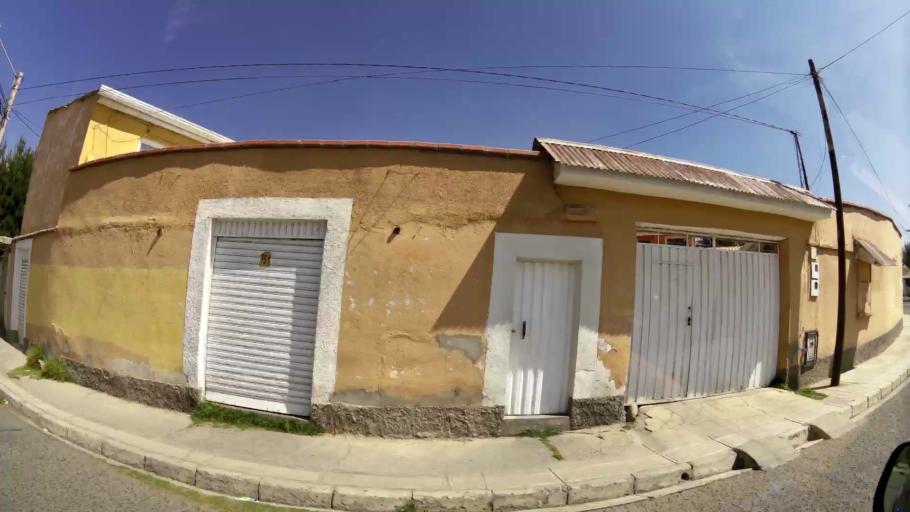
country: BO
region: La Paz
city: La Paz
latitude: -16.5384
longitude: -68.0985
